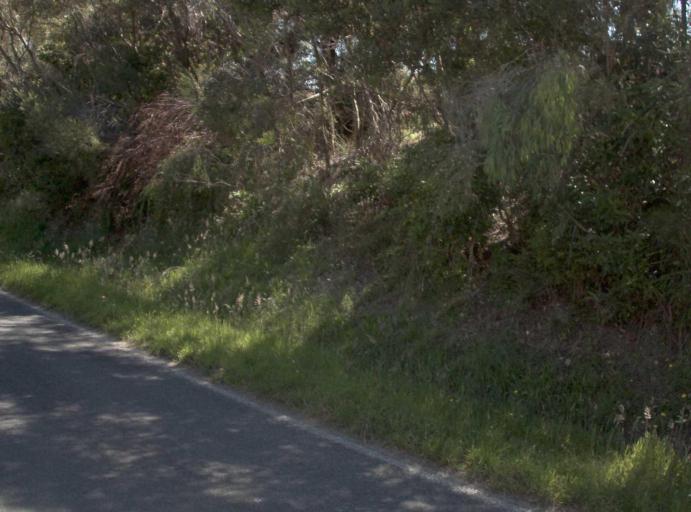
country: AU
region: Victoria
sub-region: Latrobe
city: Morwell
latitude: -38.6591
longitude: 146.1919
